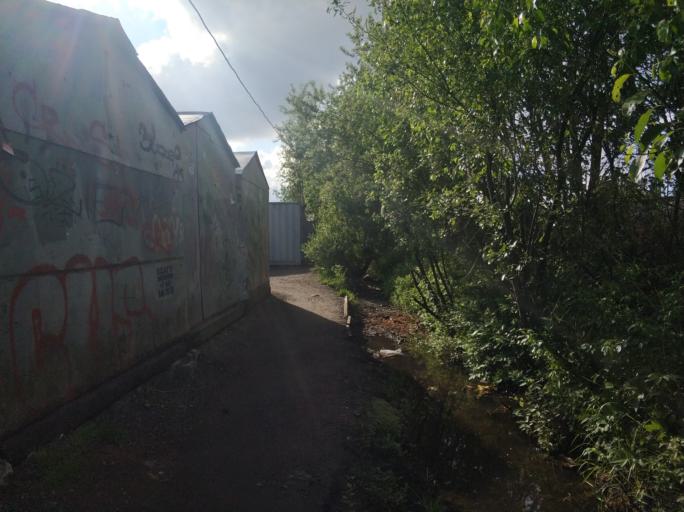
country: RU
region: Leningrad
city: Murino
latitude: 60.0433
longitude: 30.4292
